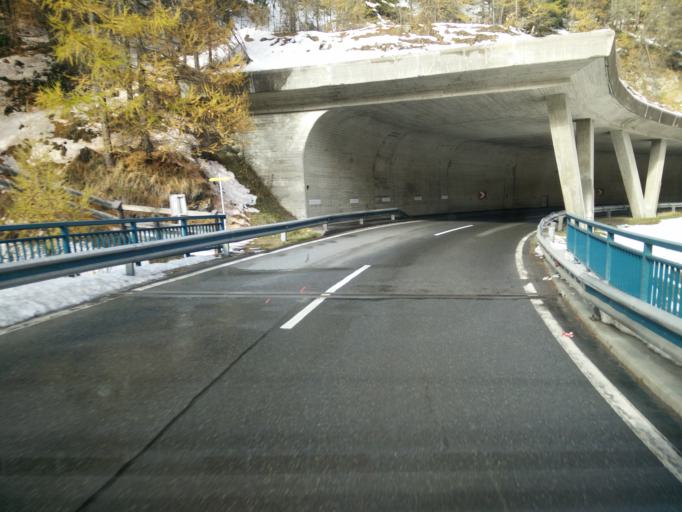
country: AT
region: Tyrol
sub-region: Politischer Bezirk Imst
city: Soelden
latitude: 46.9037
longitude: 11.0394
